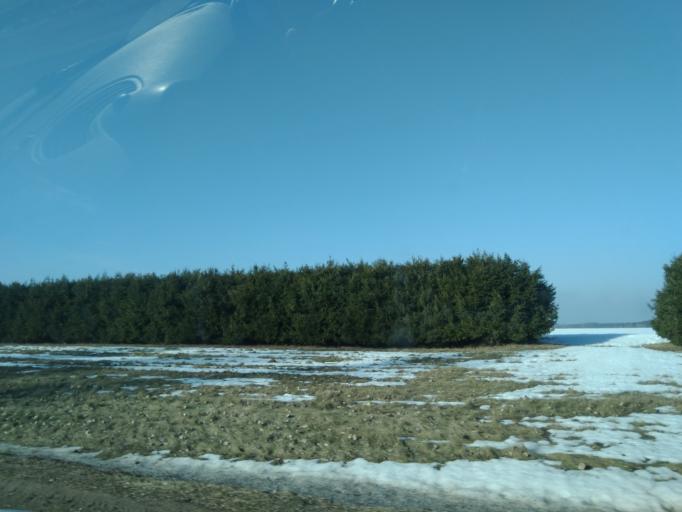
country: BY
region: Minsk
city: Nyasvizh
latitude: 53.2281
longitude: 26.6358
